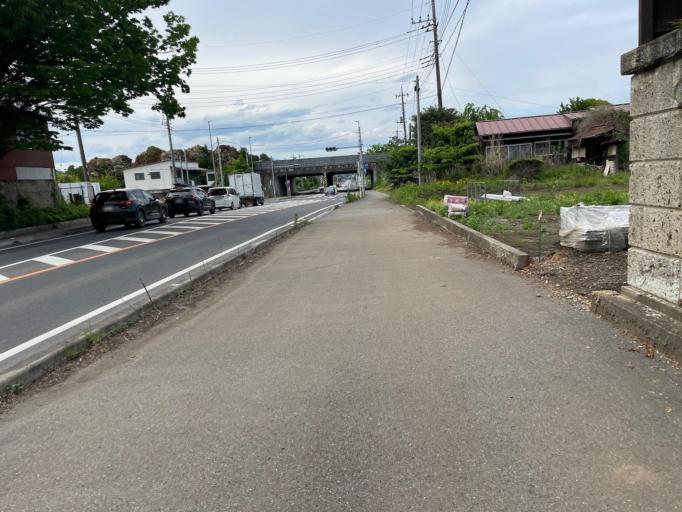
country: JP
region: Tochigi
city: Kanuma
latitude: 36.4959
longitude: 139.7543
